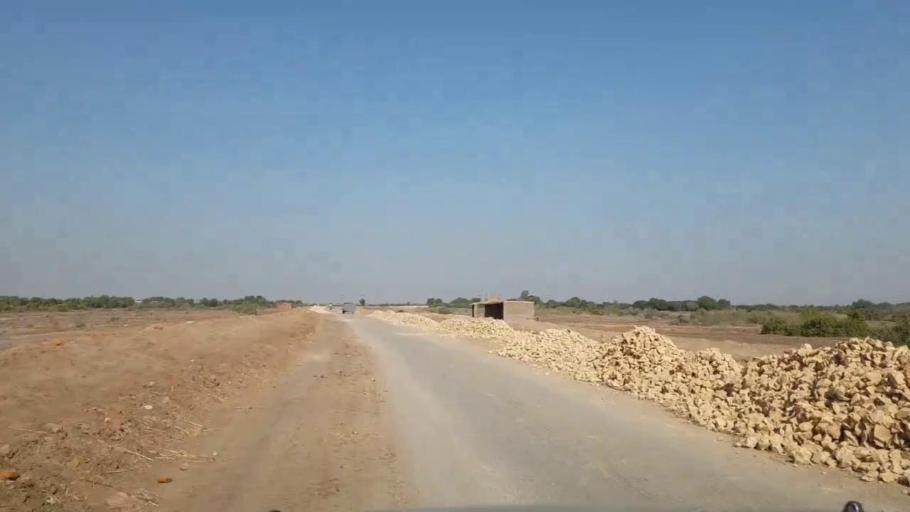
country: PK
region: Sindh
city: Digri
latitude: 24.9630
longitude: 69.1131
